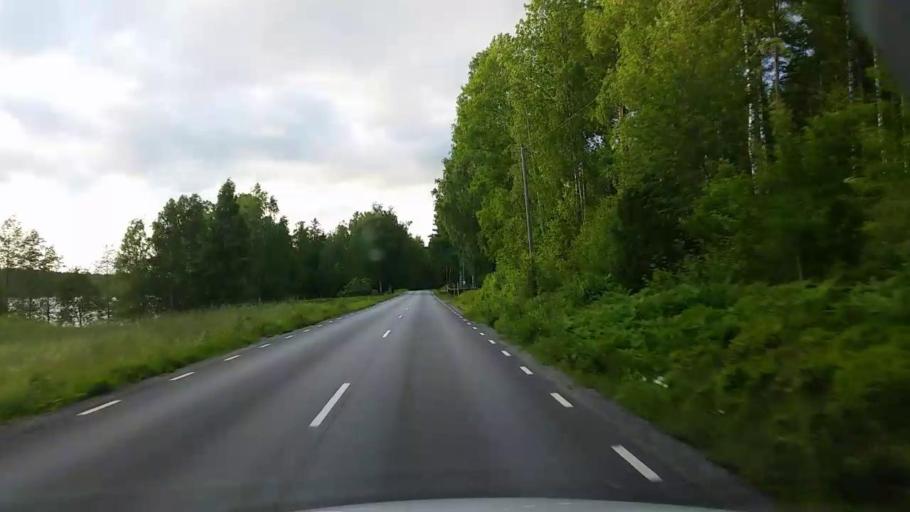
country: SE
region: Vaestmanland
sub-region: Kopings Kommun
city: Kolsva
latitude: 59.7355
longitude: 15.8255
